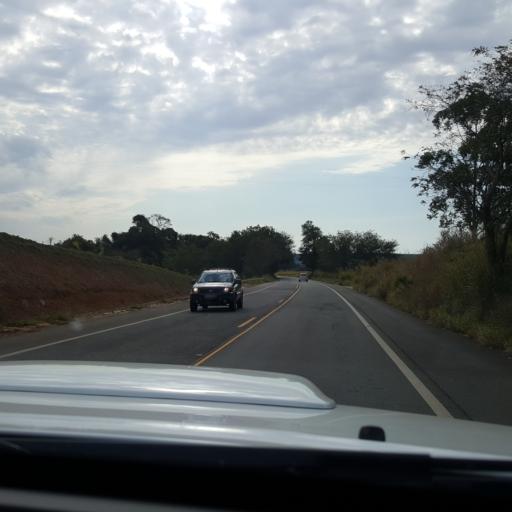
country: BR
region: Sao Paulo
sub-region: Itaporanga
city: Itaporanga
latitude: -23.7288
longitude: -49.4595
